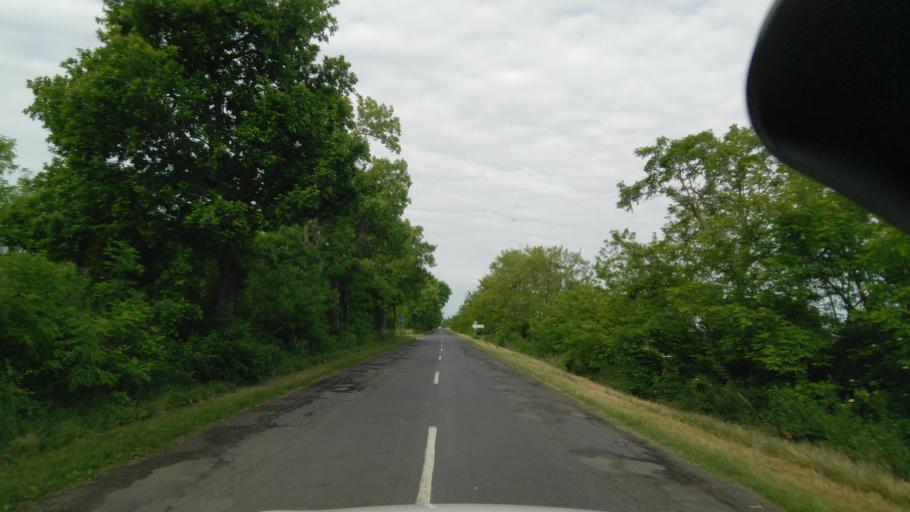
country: HU
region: Bekes
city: Ketegyhaza
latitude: 46.5331
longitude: 21.1173
